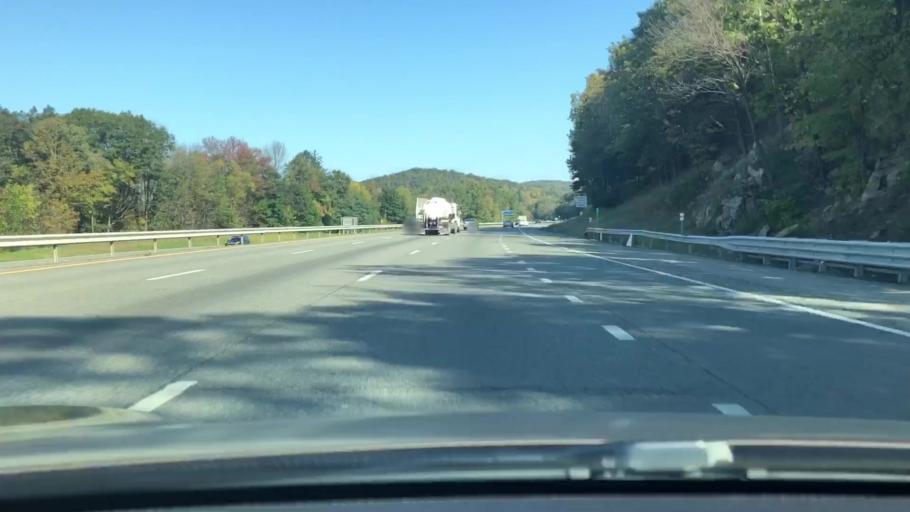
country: US
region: New York
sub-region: Rockland County
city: Sloatsburg
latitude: 41.1559
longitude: -74.1881
